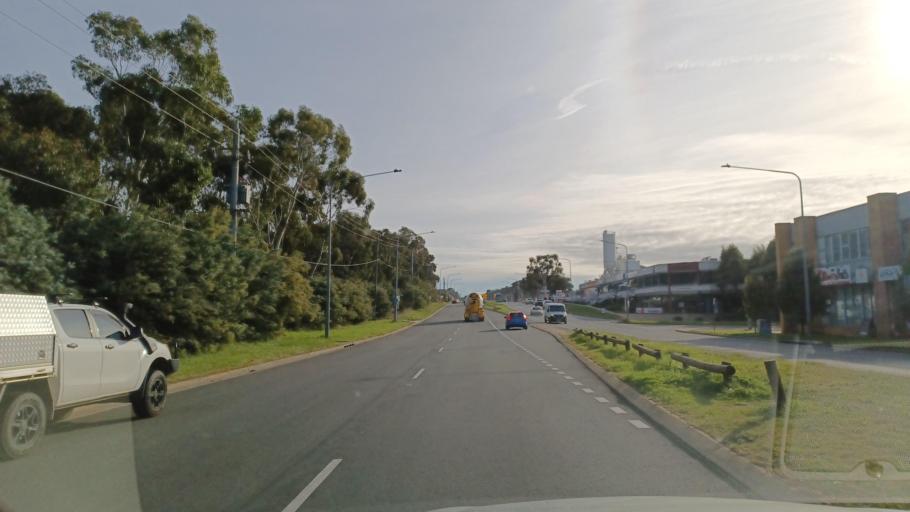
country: AU
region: Australian Capital Territory
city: Kaleen
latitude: -35.2157
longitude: 149.1374
